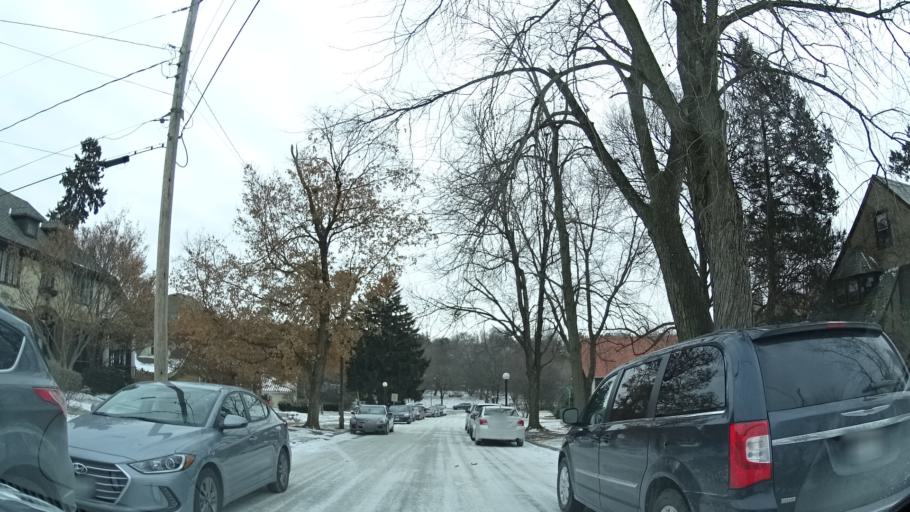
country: US
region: Nebraska
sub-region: Douglas County
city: Omaha
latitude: 41.2664
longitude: -95.9983
